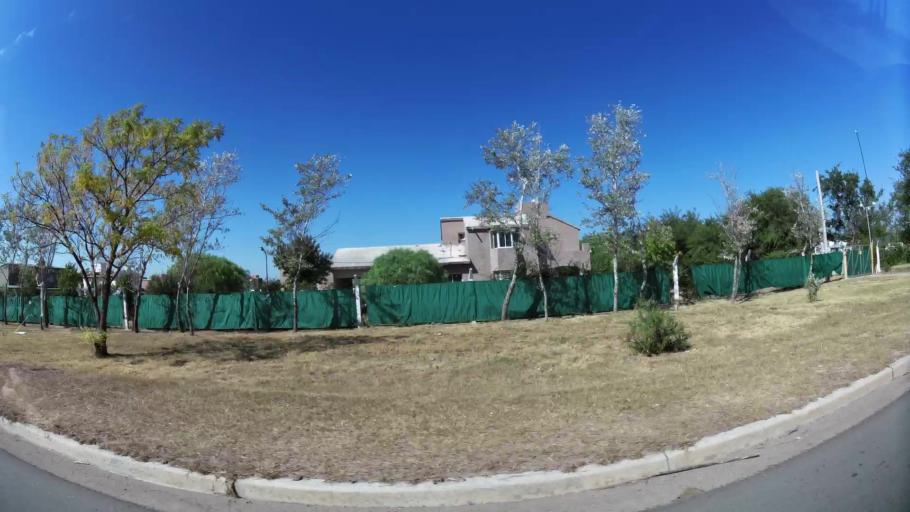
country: AR
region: Cordoba
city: Villa Allende
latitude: -31.3020
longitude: -64.2602
